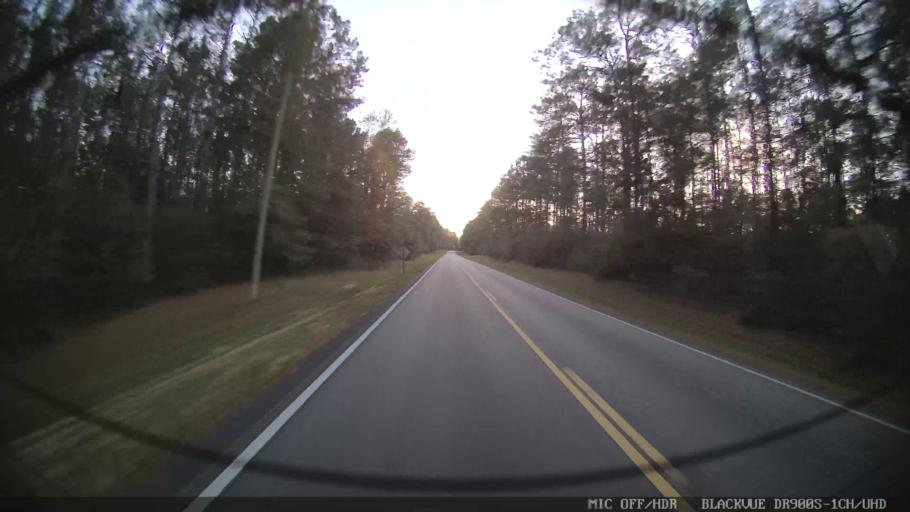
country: US
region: Mississippi
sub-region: Stone County
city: Wiggins
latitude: 31.0405
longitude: -89.2139
